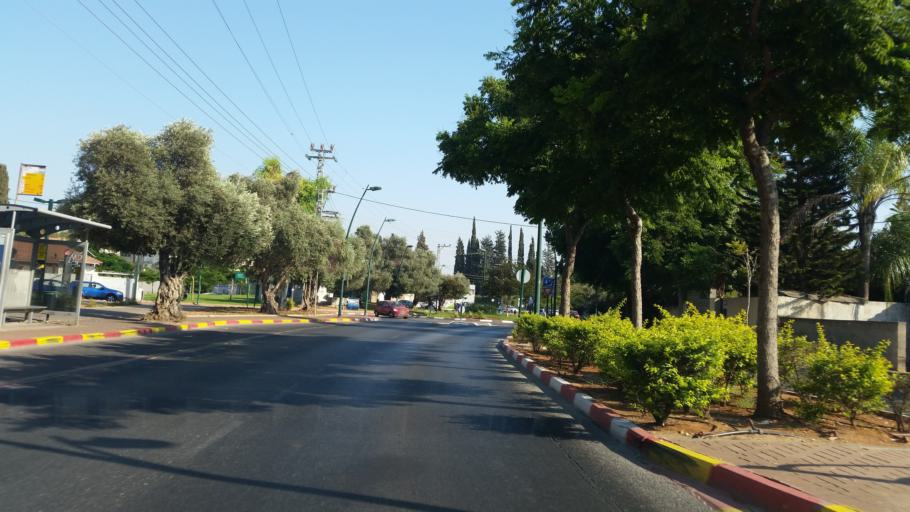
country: IL
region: Tel Aviv
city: Ramat HaSharon
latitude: 32.1297
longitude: 34.8556
